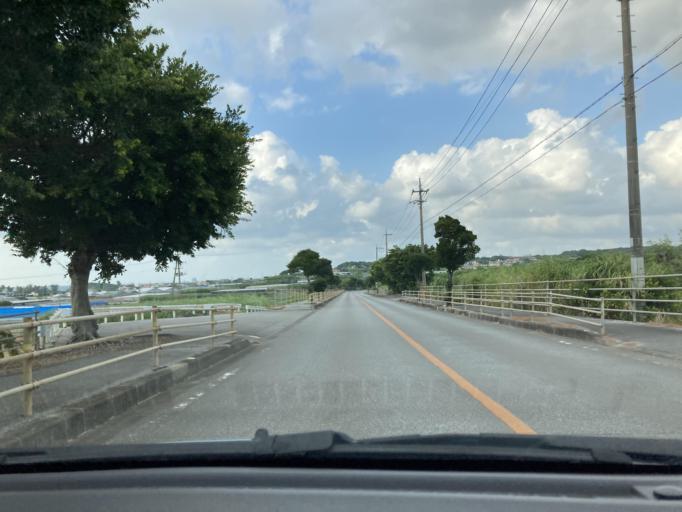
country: JP
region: Okinawa
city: Itoman
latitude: 26.0967
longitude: 127.6656
